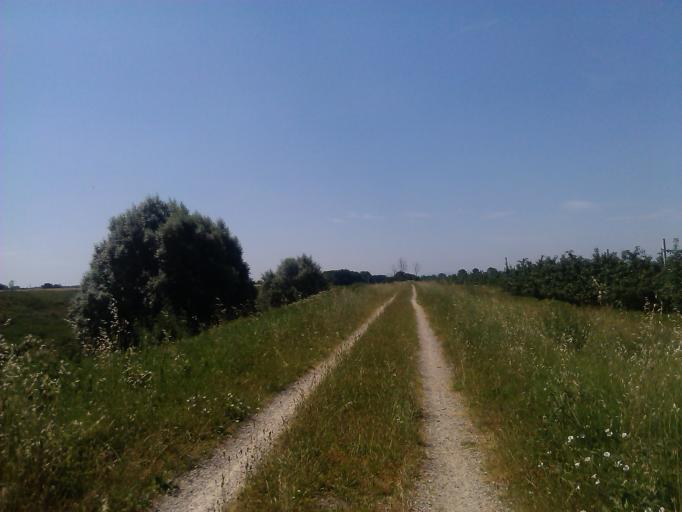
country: IT
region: Tuscany
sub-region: Province of Arezzo
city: Tegoleto
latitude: 43.3671
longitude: 11.8260
